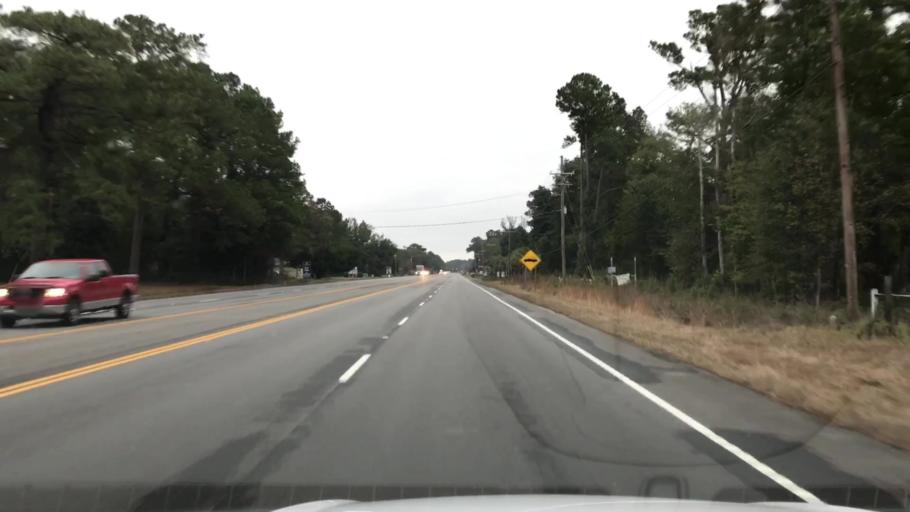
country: US
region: South Carolina
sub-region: Charleston County
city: Awendaw
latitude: 33.0905
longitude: -79.4834
